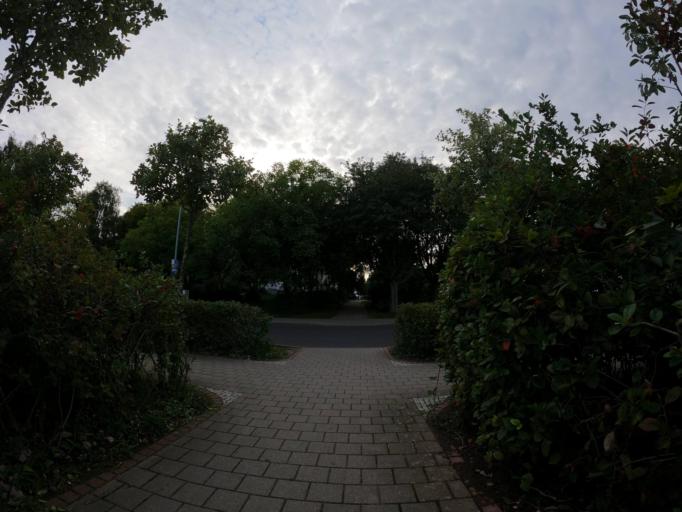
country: DE
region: Mecklenburg-Vorpommern
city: Kramerhof
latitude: 54.3280
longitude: 13.0544
